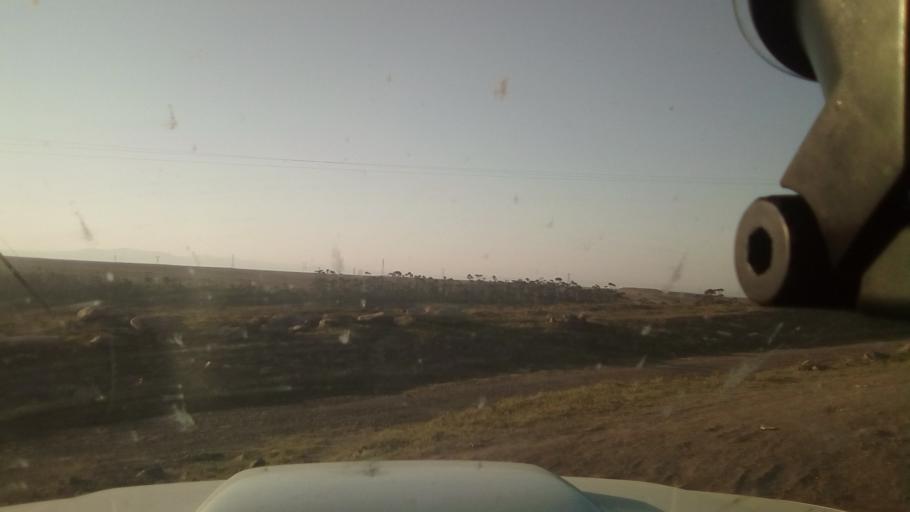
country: ZA
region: Eastern Cape
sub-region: Buffalo City Metropolitan Municipality
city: Bhisho
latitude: -32.9724
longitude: 27.2935
